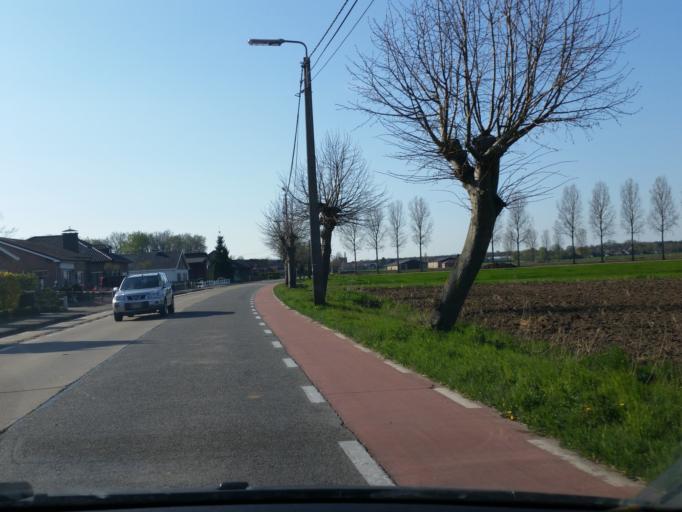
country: BE
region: Flanders
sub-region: Provincie Oost-Vlaanderen
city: Sint-Gillis-Waas
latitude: 51.2422
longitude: 4.0960
